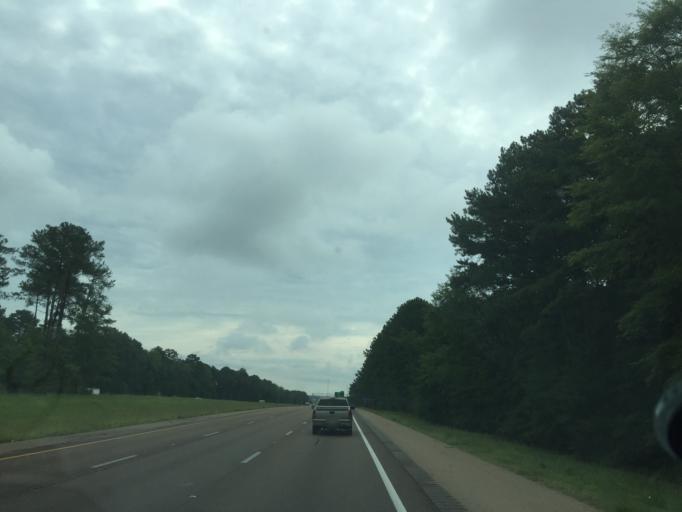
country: US
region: Mississippi
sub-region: Rankin County
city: Brandon
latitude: 32.2744
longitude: -90.0515
